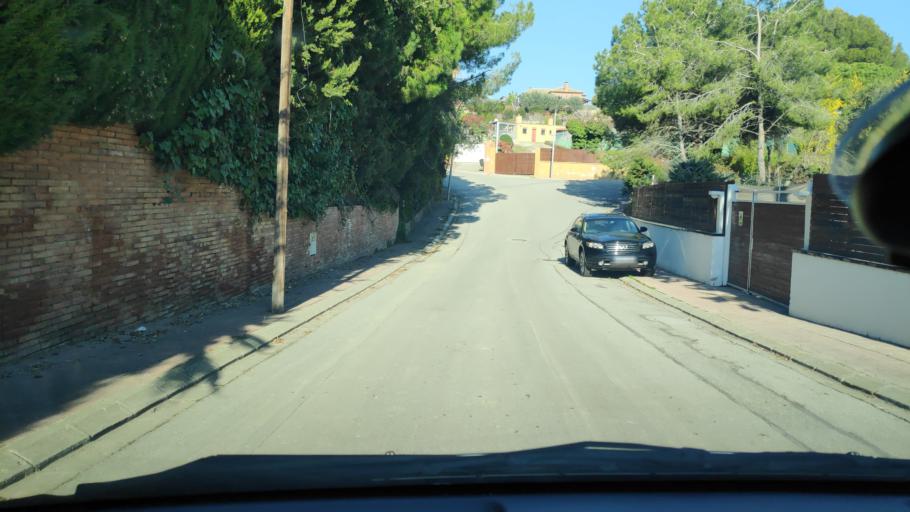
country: ES
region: Catalonia
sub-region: Provincia de Barcelona
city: Sant Quirze del Valles
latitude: 41.5065
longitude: 2.0833
